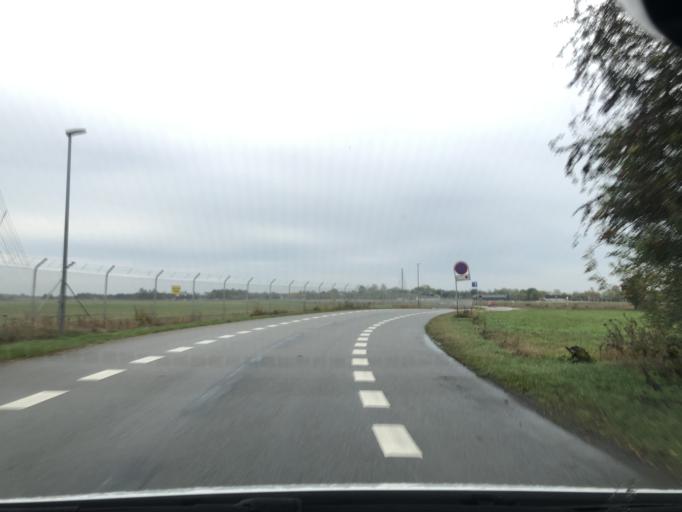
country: DK
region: Capital Region
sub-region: Tarnby Kommune
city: Tarnby
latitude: 55.5902
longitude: 12.5962
